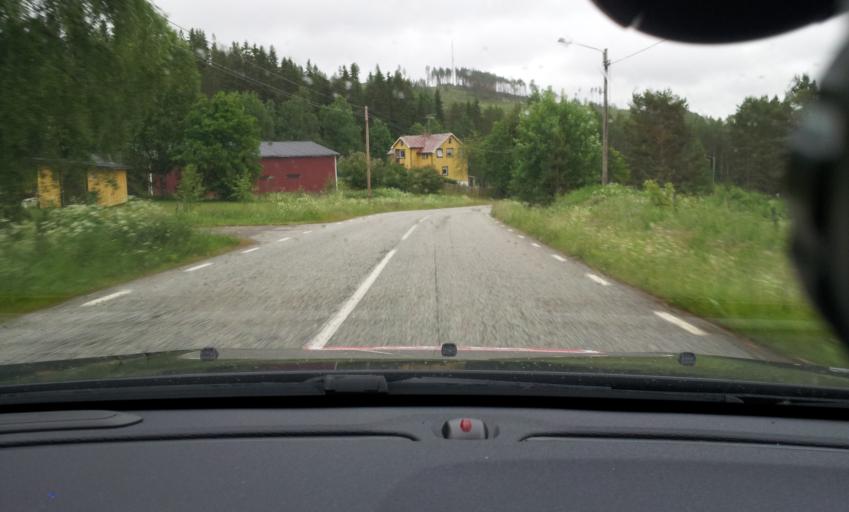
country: SE
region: Jaemtland
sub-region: Stroemsunds Kommun
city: Stroemsund
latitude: 63.3397
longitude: 15.7619
